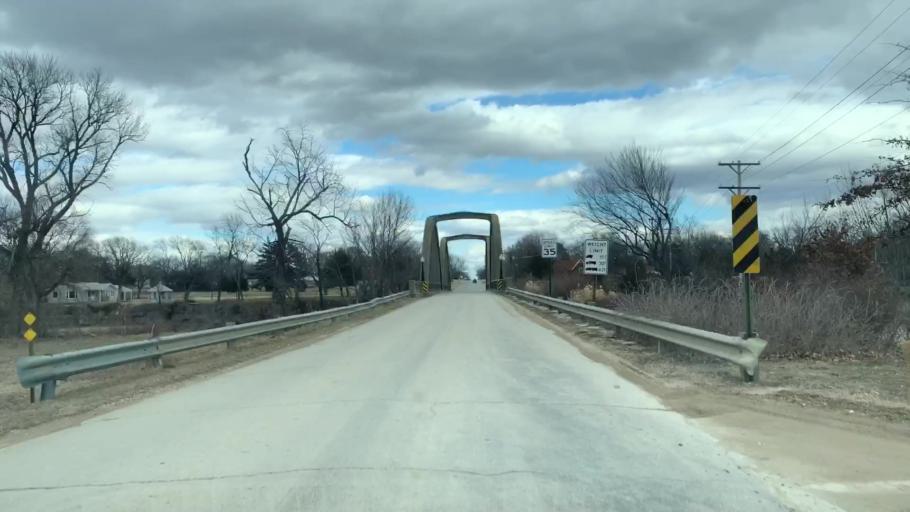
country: US
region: Kansas
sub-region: Allen County
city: Humboldt
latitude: 37.8111
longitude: -95.4490
